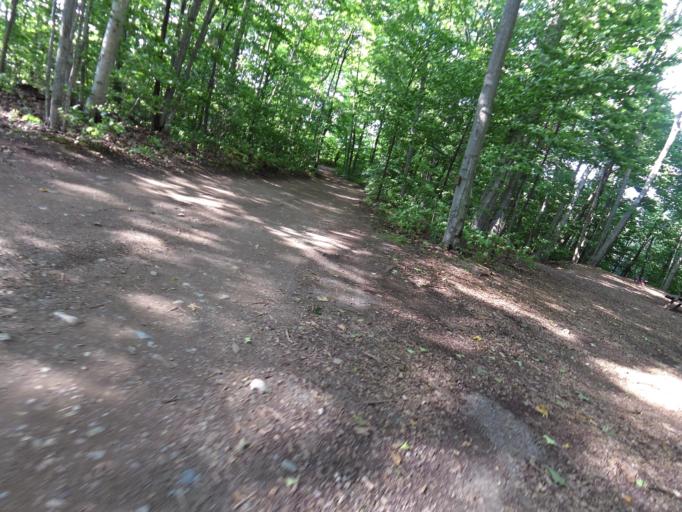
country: CA
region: Ontario
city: Tobermory
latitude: 45.2289
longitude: -81.6470
